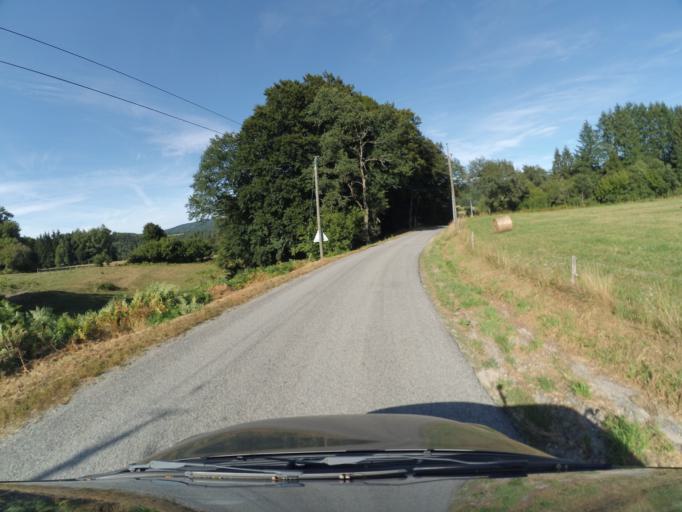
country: FR
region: Limousin
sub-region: Departement de la Correze
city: Bugeat
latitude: 45.6865
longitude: 1.8935
